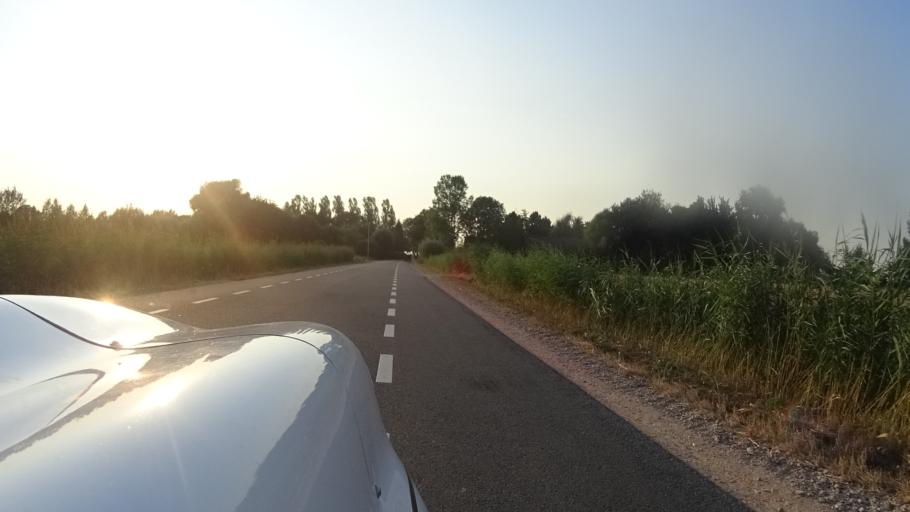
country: NL
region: Gelderland
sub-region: Gemeente Tiel
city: Tiel
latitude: 51.9310
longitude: 5.4317
